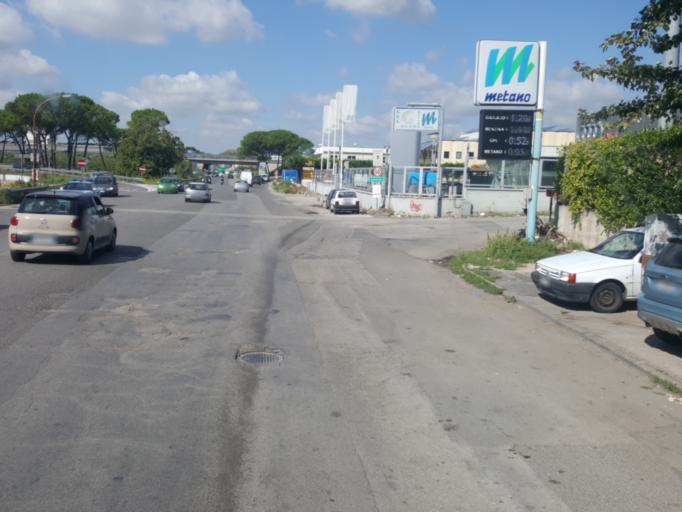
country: IT
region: Campania
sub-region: Provincia di Napoli
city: Cimitile
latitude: 40.9334
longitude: 14.5029
